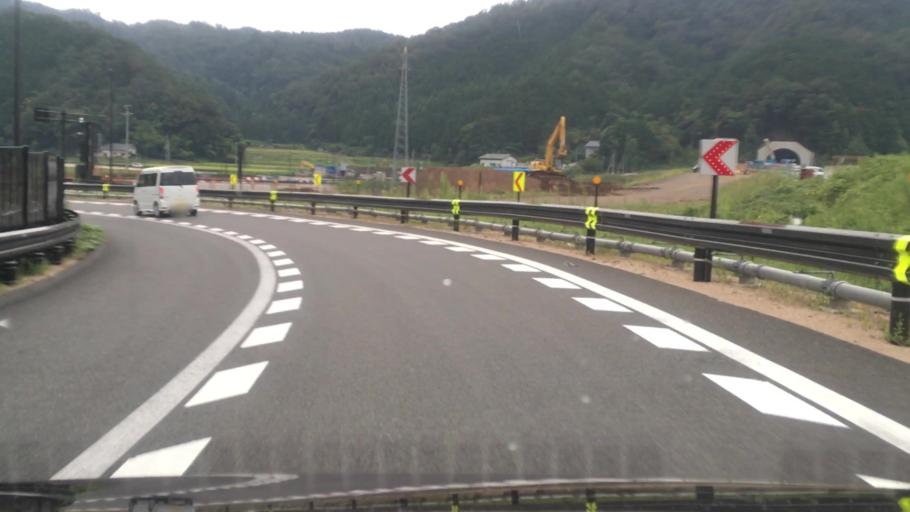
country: JP
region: Hyogo
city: Toyooka
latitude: 35.4662
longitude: 134.7633
